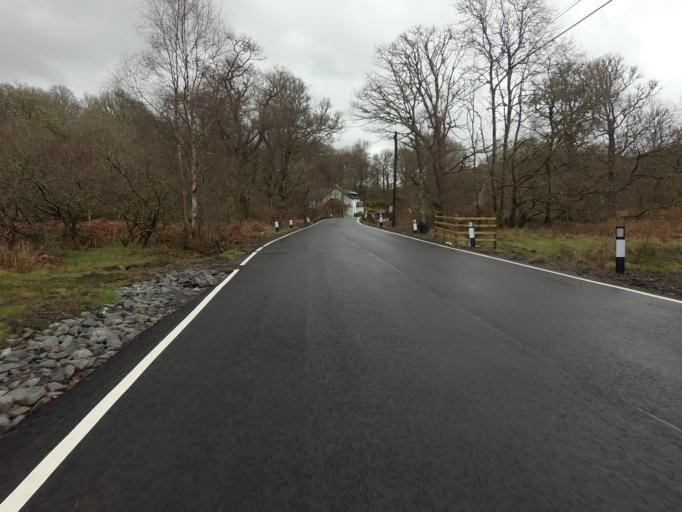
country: GB
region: Scotland
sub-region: West Dunbartonshire
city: Balloch
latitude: 56.1950
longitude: -4.5165
